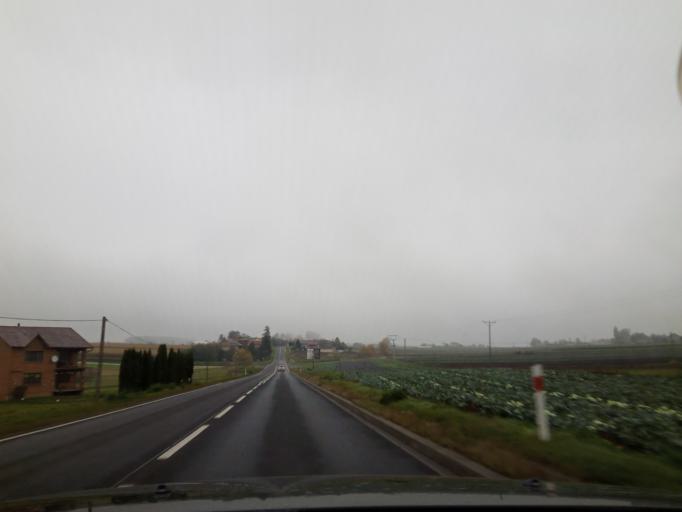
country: PL
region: Lesser Poland Voivodeship
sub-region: Powiat proszowicki
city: Proszowice
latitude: 50.1639
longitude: 20.2076
